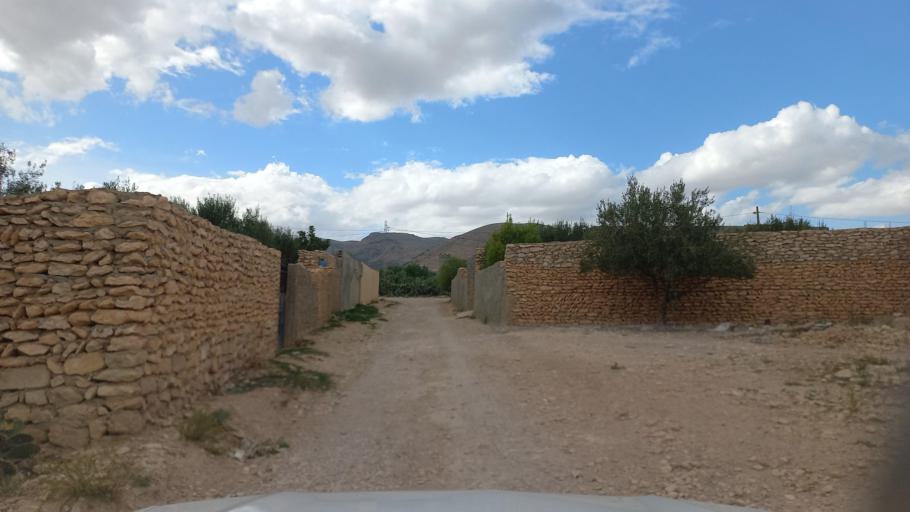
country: TN
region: Al Qasrayn
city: Sbiba
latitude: 35.4461
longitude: 9.0811
